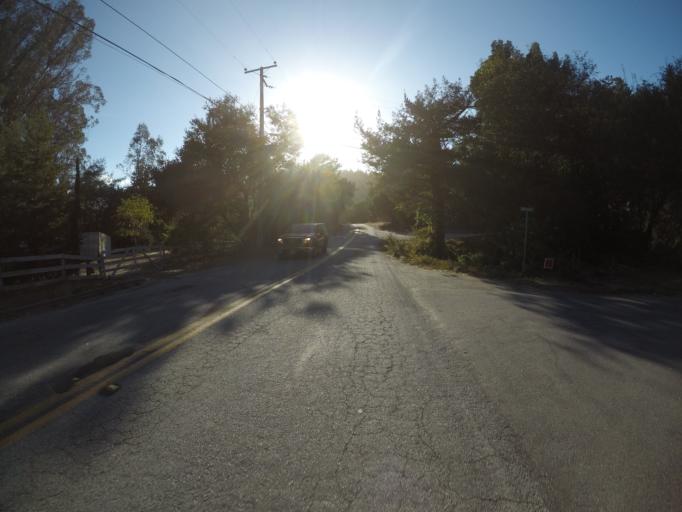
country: US
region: California
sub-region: Santa Cruz County
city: Pasatiempo
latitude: 37.0264
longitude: -122.0268
